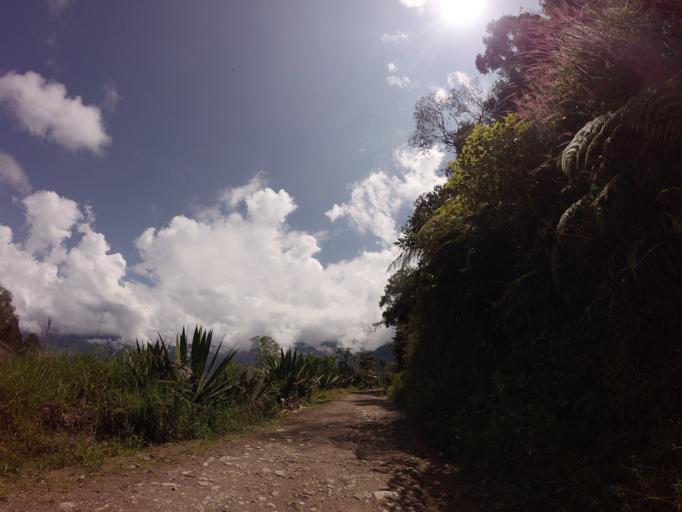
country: CO
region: Caldas
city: Pensilvania
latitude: 5.4792
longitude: -75.1855
